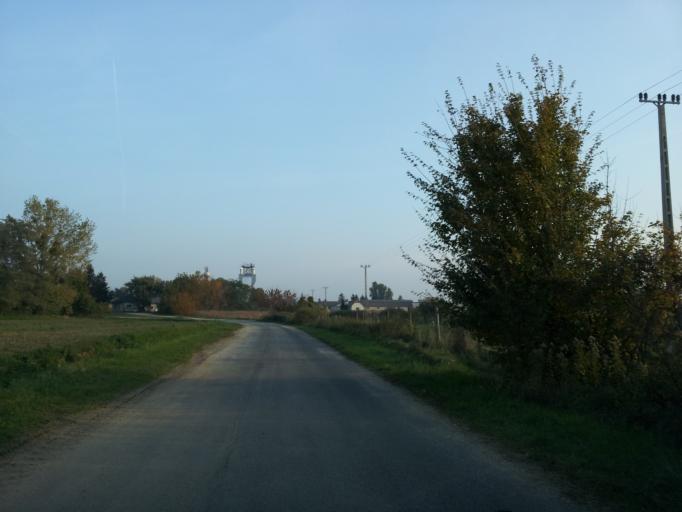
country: HU
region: Komarom-Esztergom
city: Kisber
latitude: 47.4683
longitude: 17.9548
